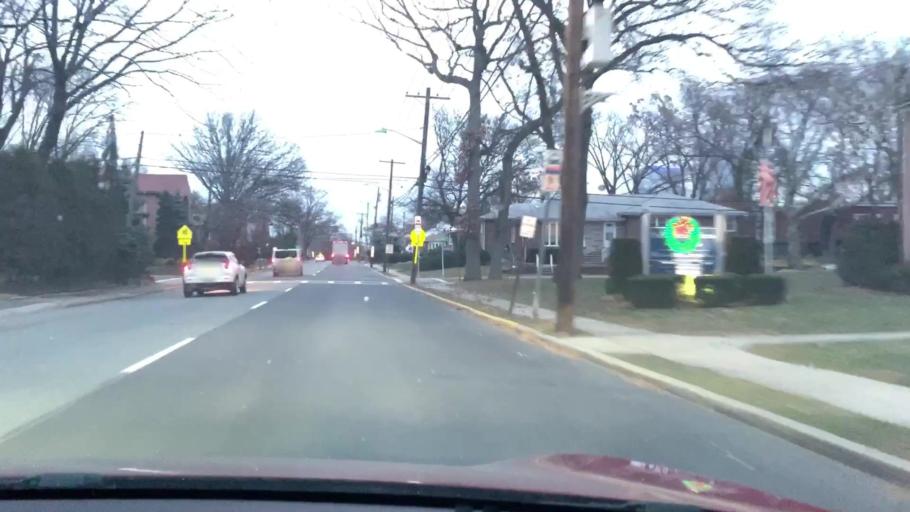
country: US
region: New Jersey
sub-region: Bergen County
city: Fort Lee
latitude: 40.8464
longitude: -73.9774
